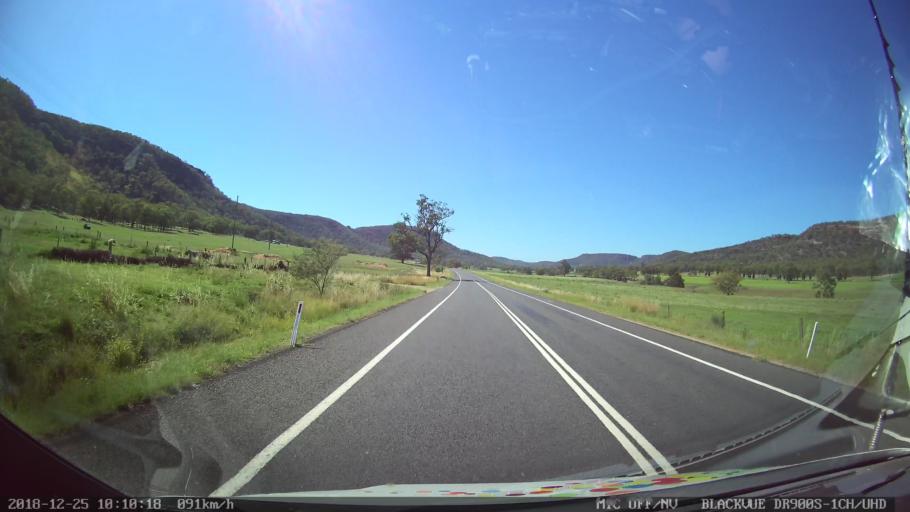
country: AU
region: New South Wales
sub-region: Muswellbrook
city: Denman
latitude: -32.3021
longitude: 150.5211
